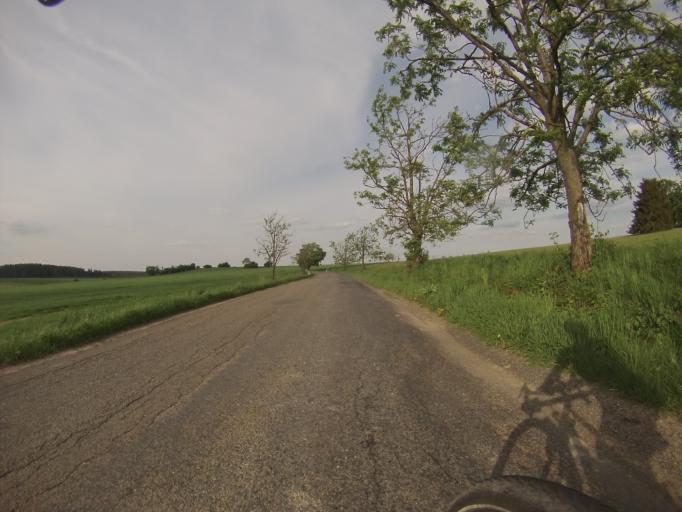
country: CZ
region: Olomoucky
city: Protivanov
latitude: 49.4381
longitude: 16.8370
